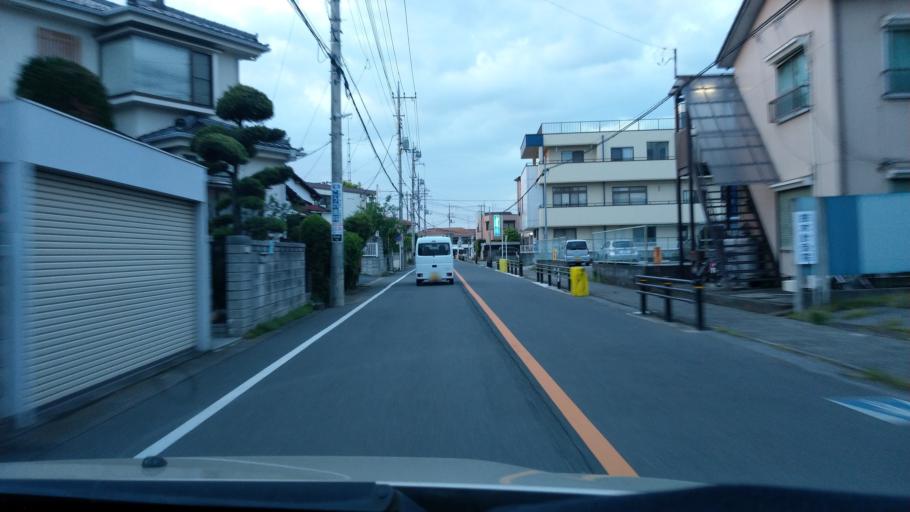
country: JP
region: Saitama
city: Iwatsuki
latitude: 35.9554
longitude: 139.6967
